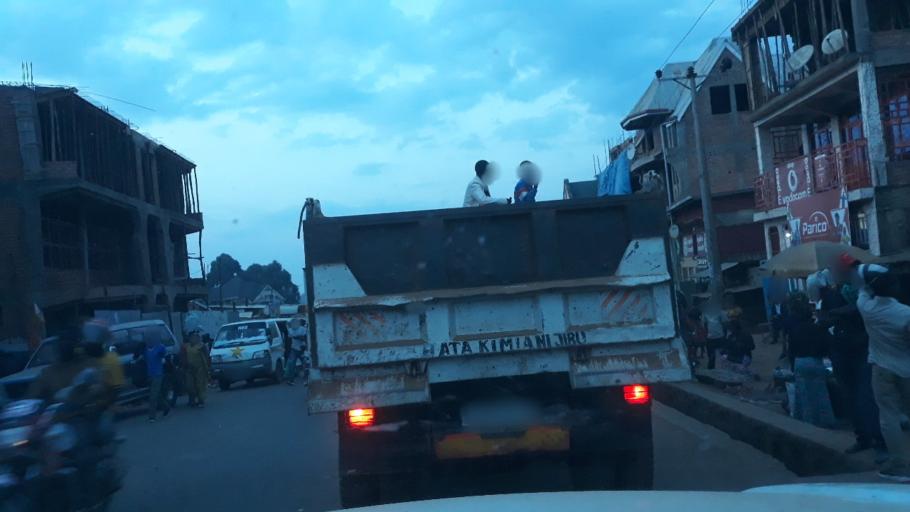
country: CD
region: South Kivu
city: Bukavu
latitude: -2.5236
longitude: 28.8539
